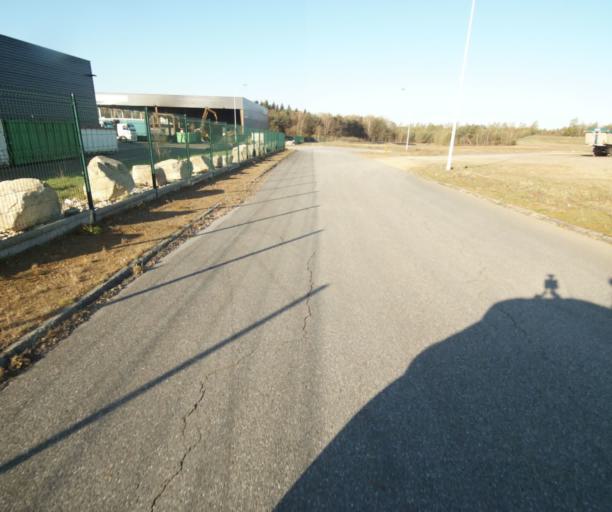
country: FR
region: Limousin
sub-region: Departement de la Correze
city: Correze
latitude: 45.3330
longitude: 1.8982
